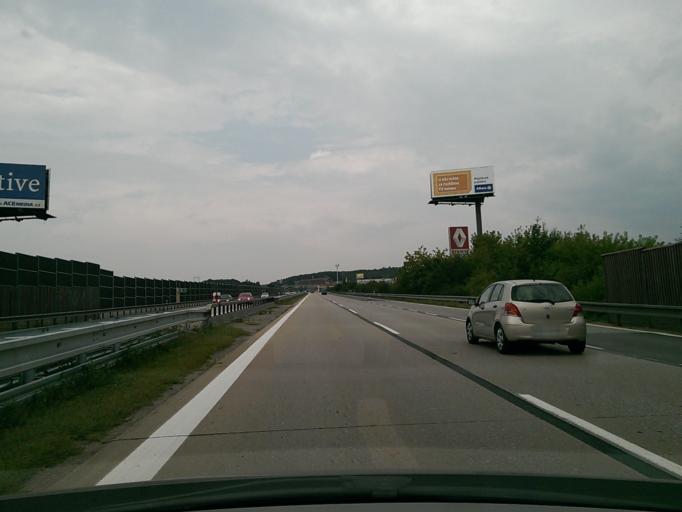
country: CZ
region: South Moravian
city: Troubsko
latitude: 49.1793
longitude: 16.4886
